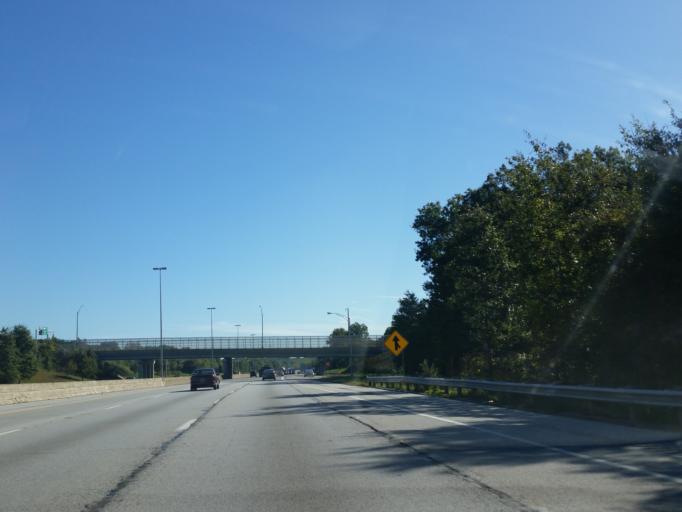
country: US
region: Ohio
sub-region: Cuyahoga County
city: Bay Village
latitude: 41.4755
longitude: -81.8851
